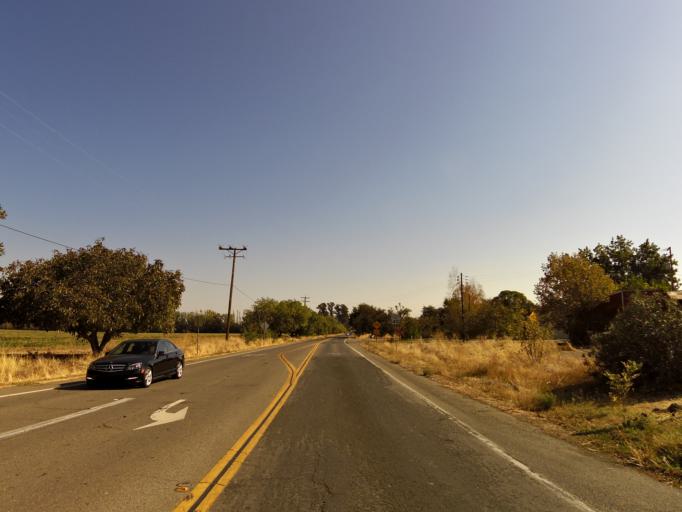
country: US
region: California
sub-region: Solano County
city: Green Valley
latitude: 38.2441
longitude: -122.1215
